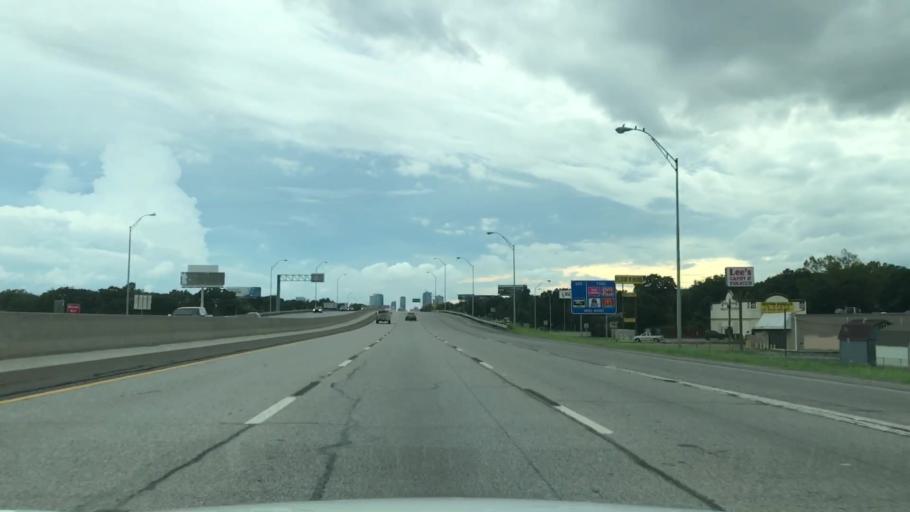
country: US
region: Texas
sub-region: Tarrant County
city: Haltom City
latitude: 32.7807
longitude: -97.2759
